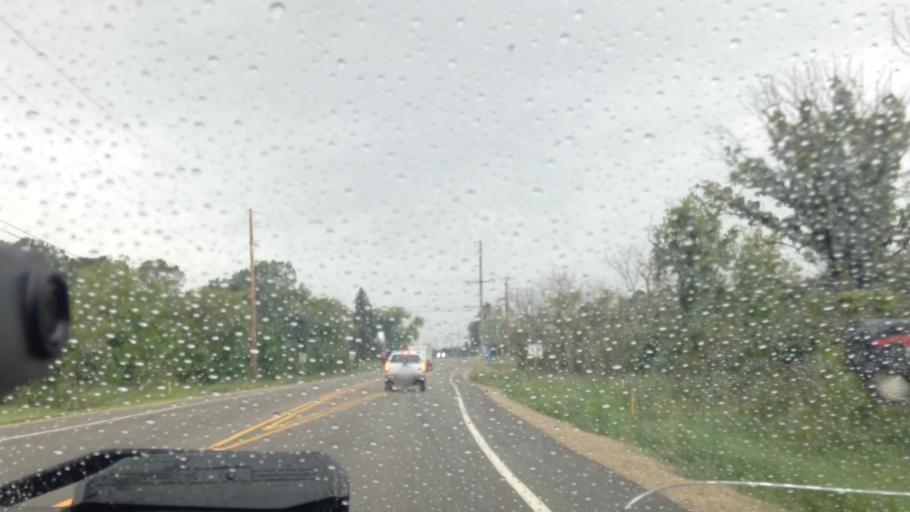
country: US
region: Wisconsin
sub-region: Washington County
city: Richfield
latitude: 43.2827
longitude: -88.2125
